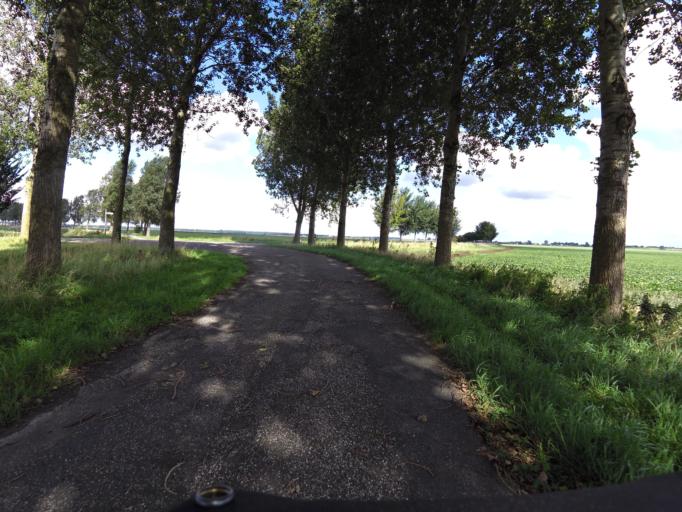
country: NL
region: South Holland
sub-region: Gemeente Goeree-Overflakkee
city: Middelharnis
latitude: 51.6971
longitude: 4.2319
